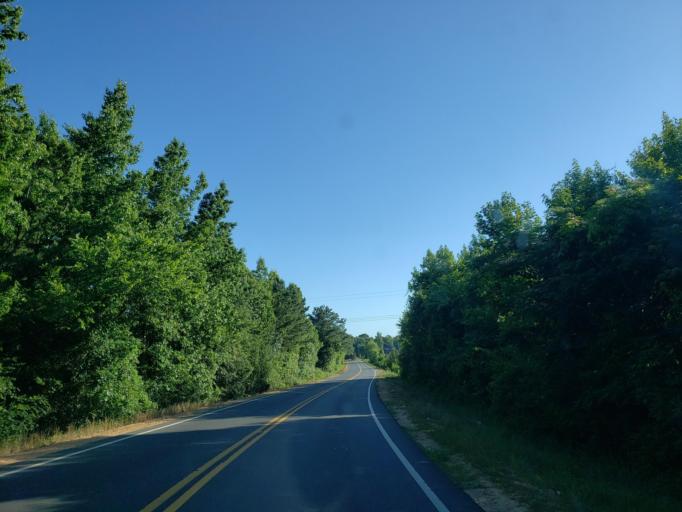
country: US
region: Georgia
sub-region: Floyd County
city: Shannon
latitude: 34.3602
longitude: -85.1409
